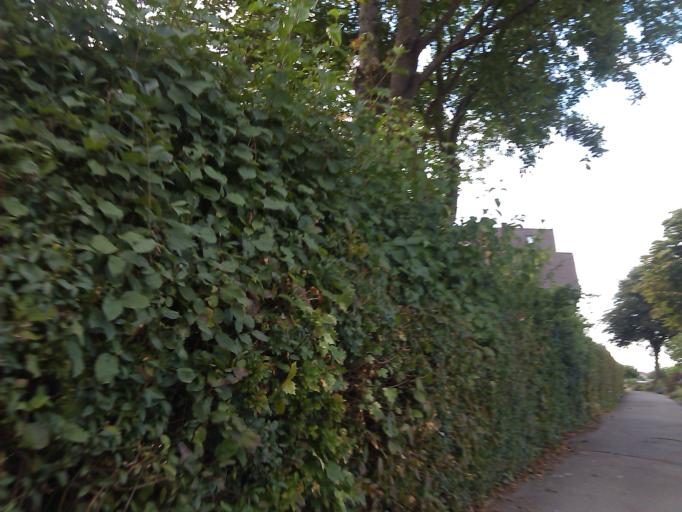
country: DE
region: Rheinland-Pfalz
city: Speyer
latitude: 49.3173
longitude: 8.4499
